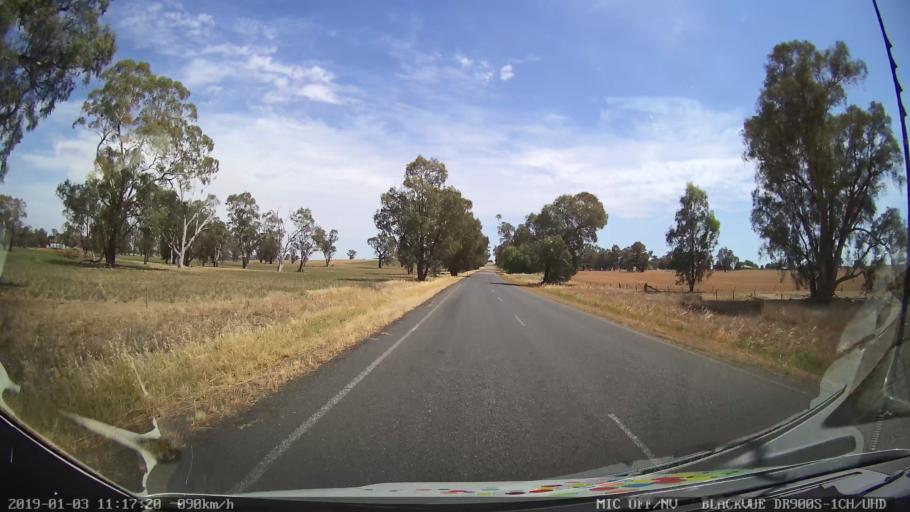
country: AU
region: New South Wales
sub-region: Young
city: Young
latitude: -34.1399
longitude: 148.2664
